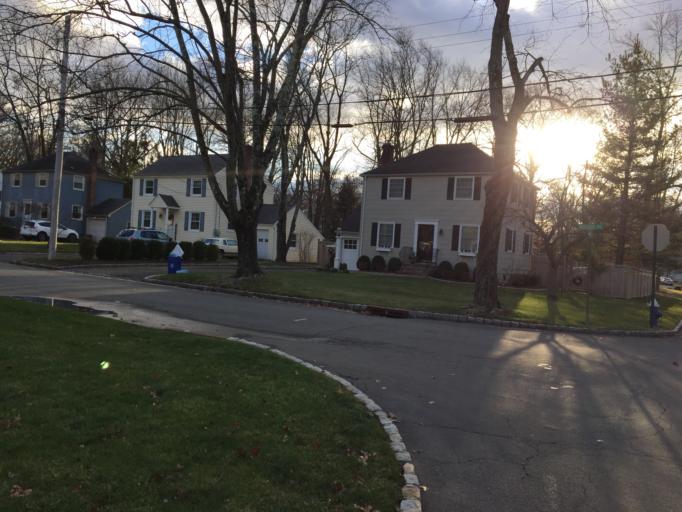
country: US
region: New Jersey
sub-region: Union County
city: New Providence
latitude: 40.7061
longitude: -74.4125
